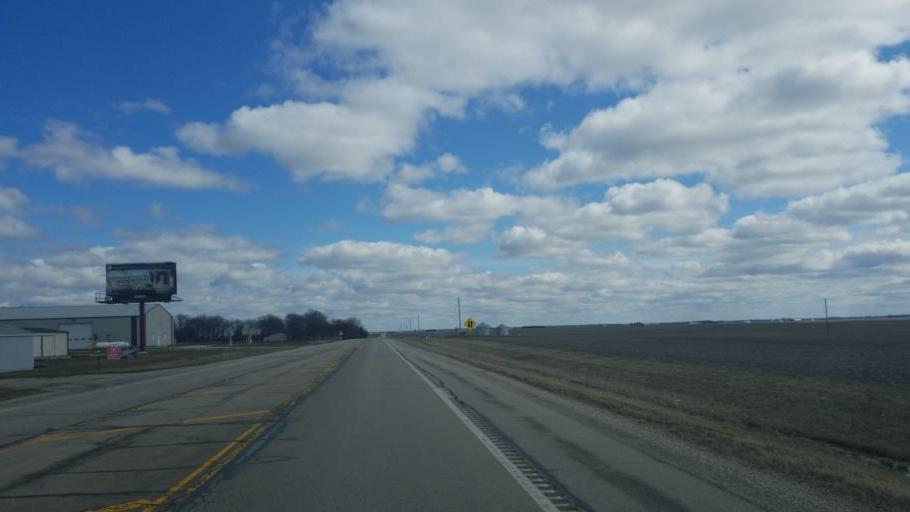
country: US
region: Illinois
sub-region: Douglas County
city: Villa Grove
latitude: 39.7917
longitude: -88.1595
